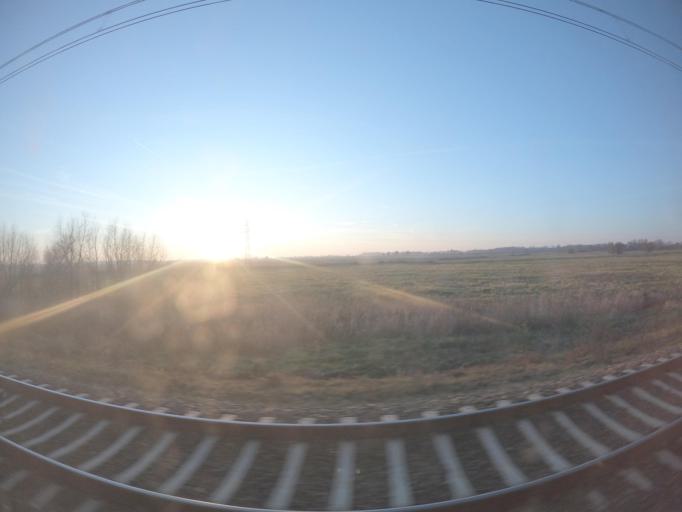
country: PL
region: Lubusz
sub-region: Powiat gorzowski
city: Kostrzyn nad Odra
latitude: 52.5592
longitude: 14.6489
